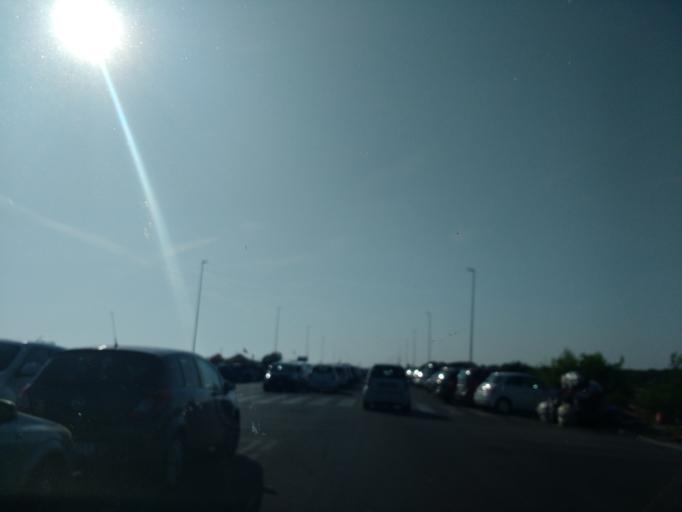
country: IT
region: Latium
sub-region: Citta metropolitana di Roma Capitale
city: Acilia-Castel Fusano-Ostia Antica
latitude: 41.7022
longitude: 12.3451
